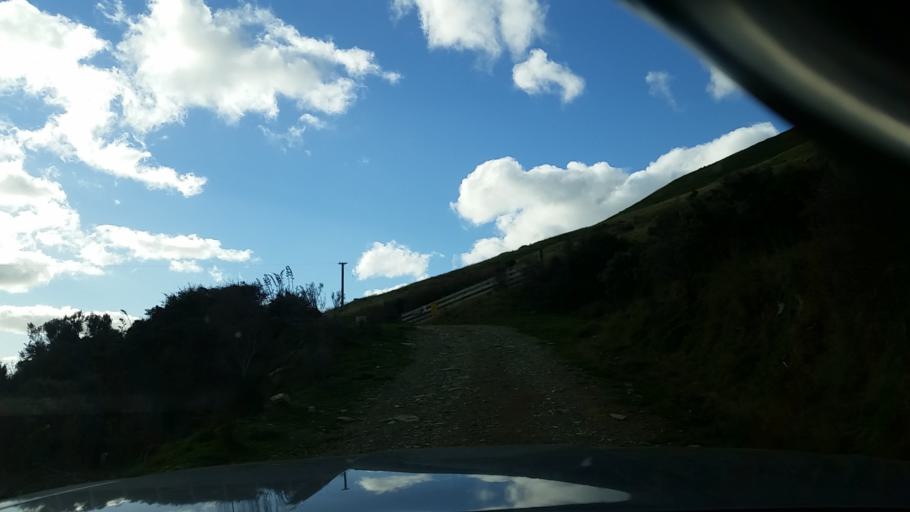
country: NZ
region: Marlborough
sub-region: Marlborough District
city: Picton
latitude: -41.0525
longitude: 174.1098
